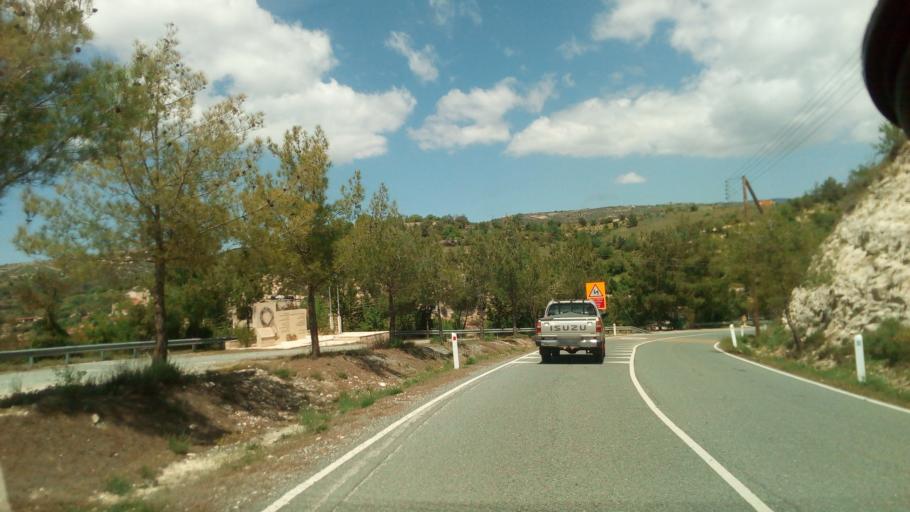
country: CY
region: Limassol
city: Pachna
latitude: 34.8380
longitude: 32.7713
